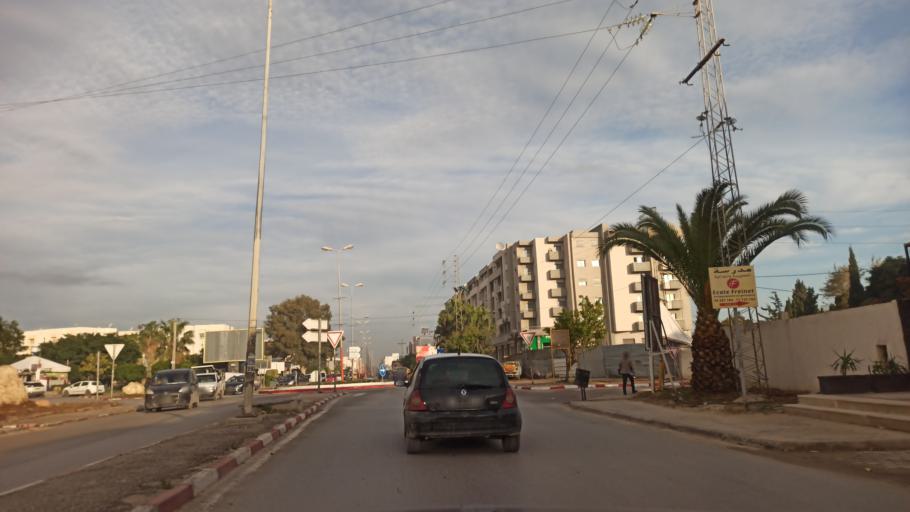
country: TN
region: Ariana
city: Ariana
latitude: 36.8614
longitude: 10.2547
